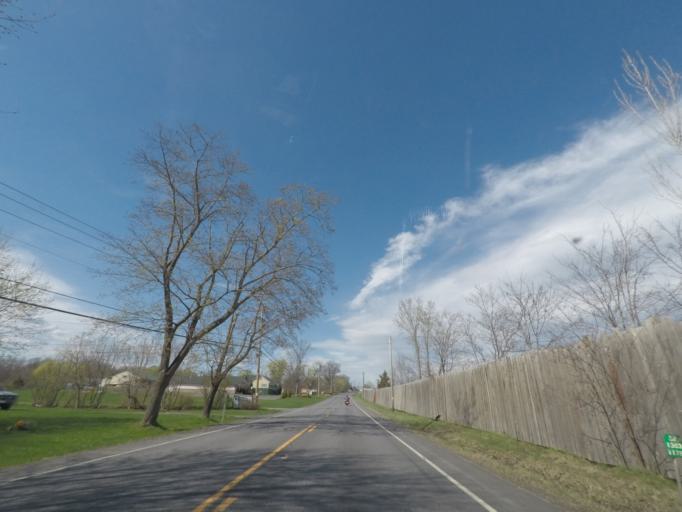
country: US
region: New York
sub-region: Greene County
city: Cairo
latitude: 42.3985
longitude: -74.0286
